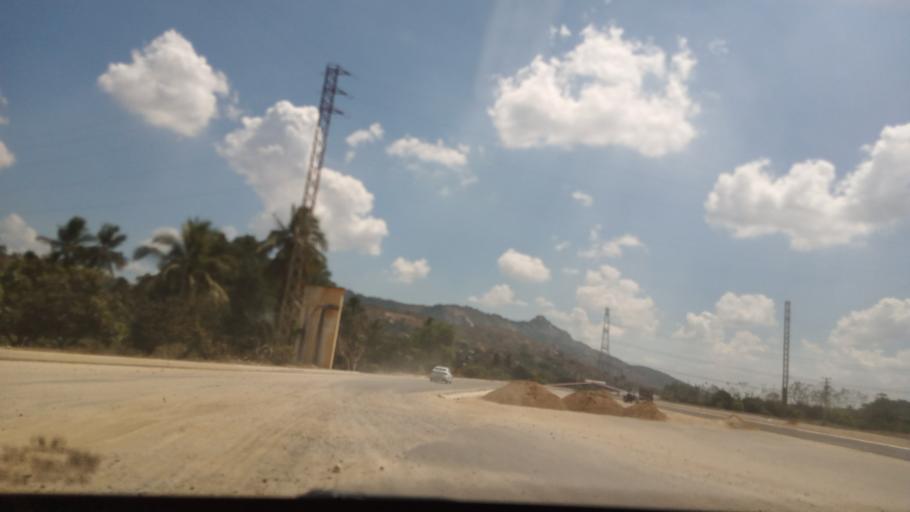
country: IN
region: Andhra Pradesh
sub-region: Chittoor
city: Pakala
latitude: 13.3441
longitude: 79.0821
